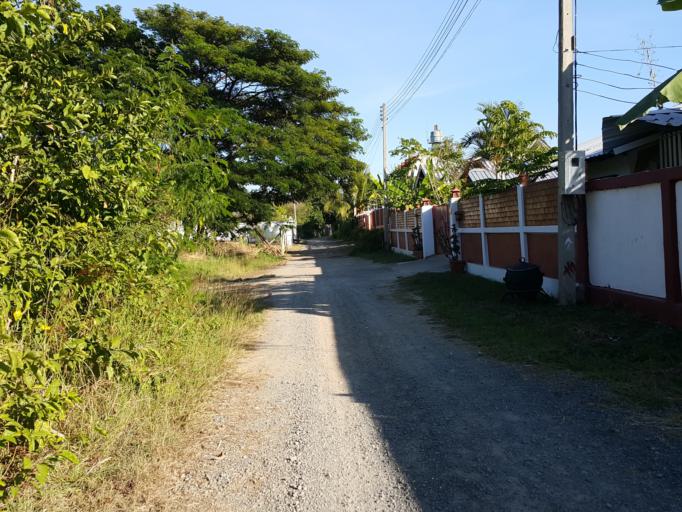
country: TH
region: Chiang Mai
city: San Kamphaeng
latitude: 18.7754
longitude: 99.0864
